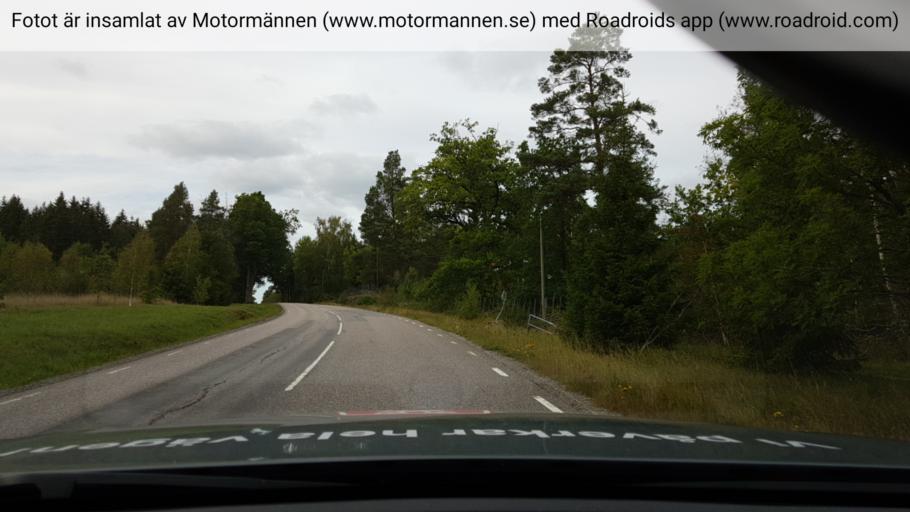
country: SE
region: Stockholm
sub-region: Haninge Kommun
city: Haninge
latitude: 59.1150
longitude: 18.1905
